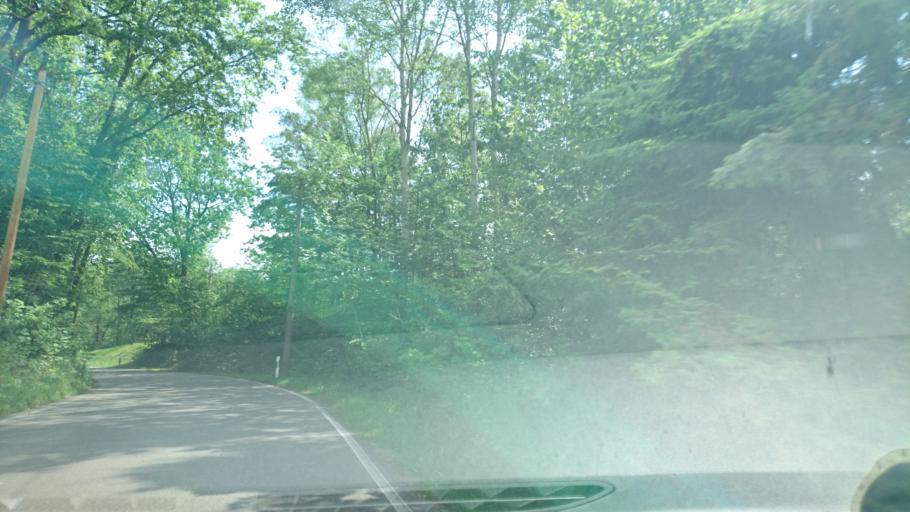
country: DE
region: Saxony
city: Dohma
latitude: 50.9132
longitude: 13.9750
